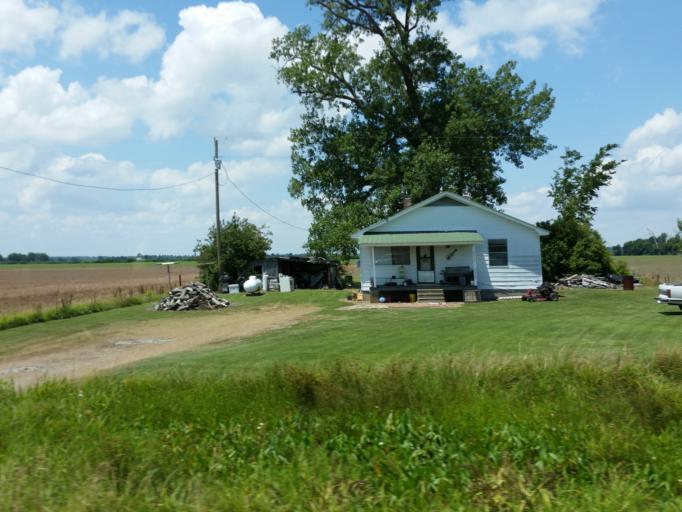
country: US
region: Kentucky
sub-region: Fulton County
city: Hickman
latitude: 36.5377
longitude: -89.3387
